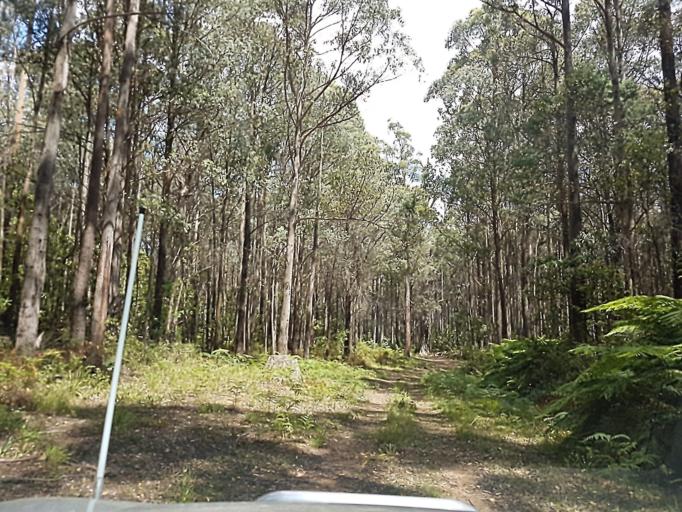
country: AU
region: Victoria
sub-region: East Gippsland
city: Lakes Entrance
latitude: -37.3290
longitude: 148.3248
